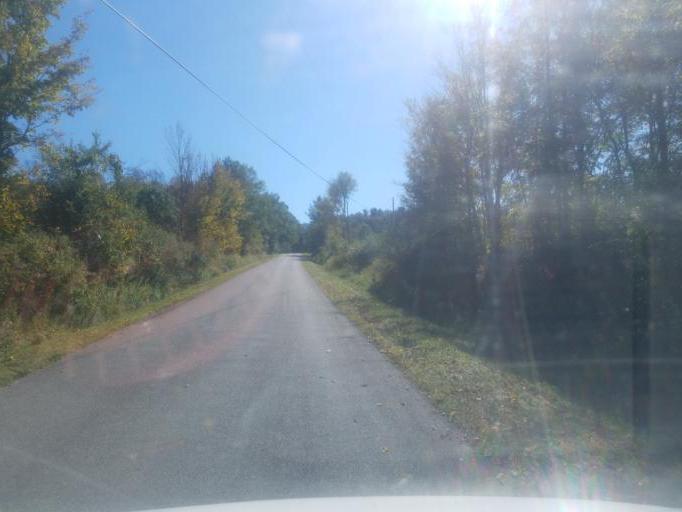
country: US
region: New York
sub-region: Allegany County
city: Houghton
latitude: 42.3187
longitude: -78.2067
